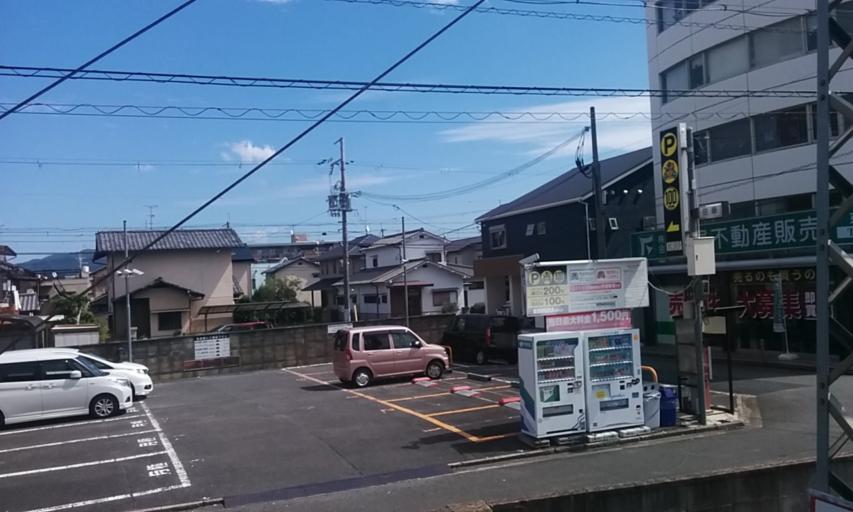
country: JP
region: Kyoto
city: Tanabe
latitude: 34.8228
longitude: 135.7734
